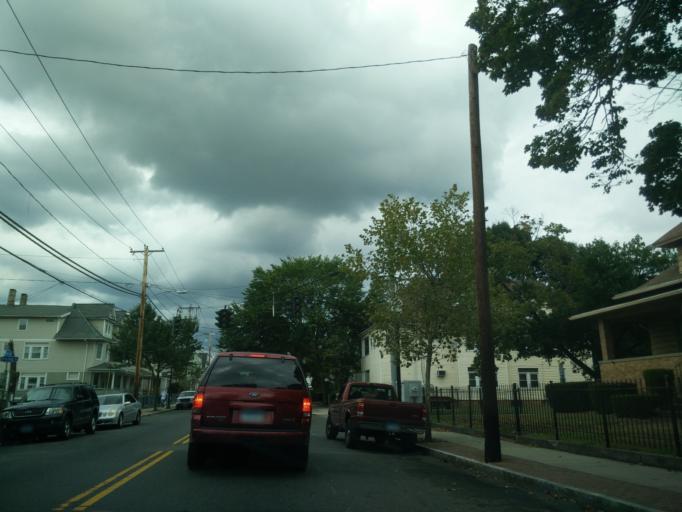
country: US
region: Connecticut
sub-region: Fairfield County
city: Bridgeport
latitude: 41.1955
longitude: -73.1804
